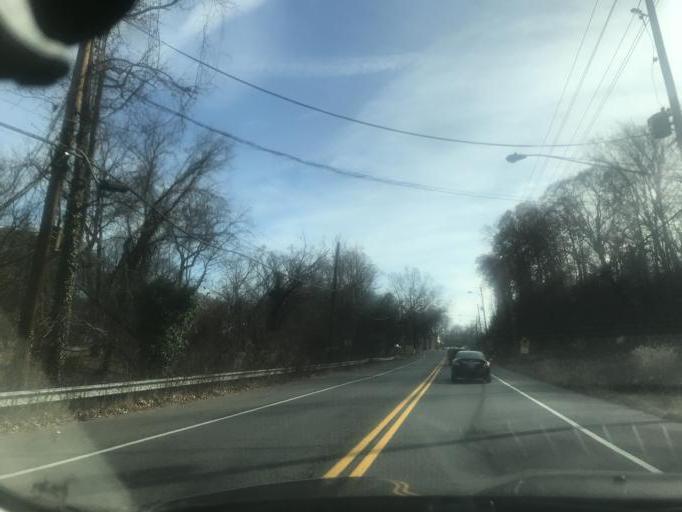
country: US
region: Maryland
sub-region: Prince George's County
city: Forest Heights
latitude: 38.8110
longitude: -76.9923
